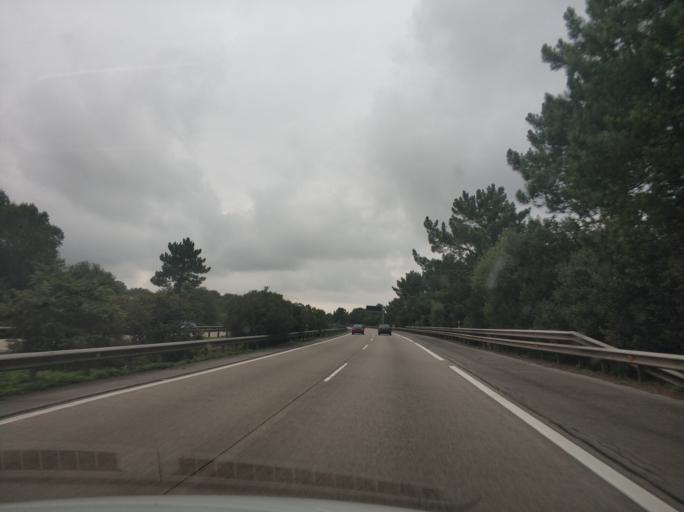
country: ES
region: Asturias
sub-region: Province of Asturias
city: Corvera de Asturias
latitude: 43.5247
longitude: -5.8244
